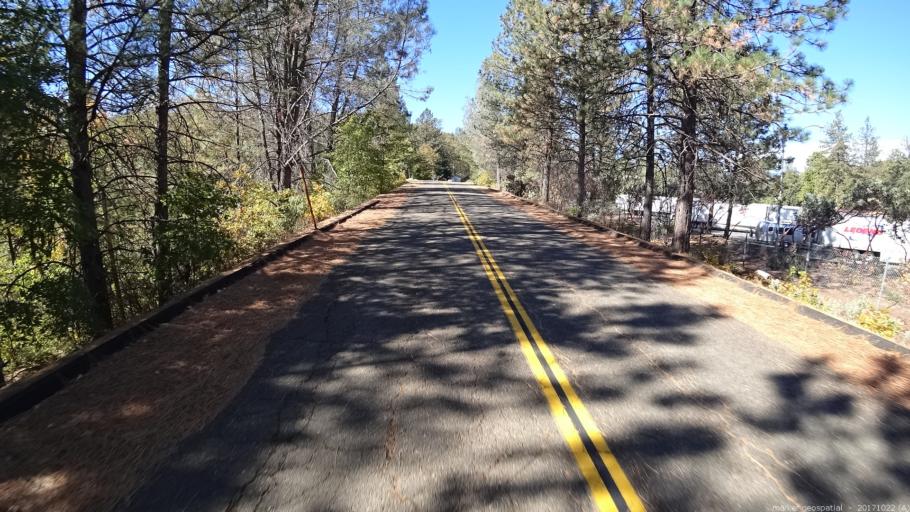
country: US
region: California
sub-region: Shasta County
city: Central Valley (historical)
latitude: 40.9164
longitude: -122.3973
